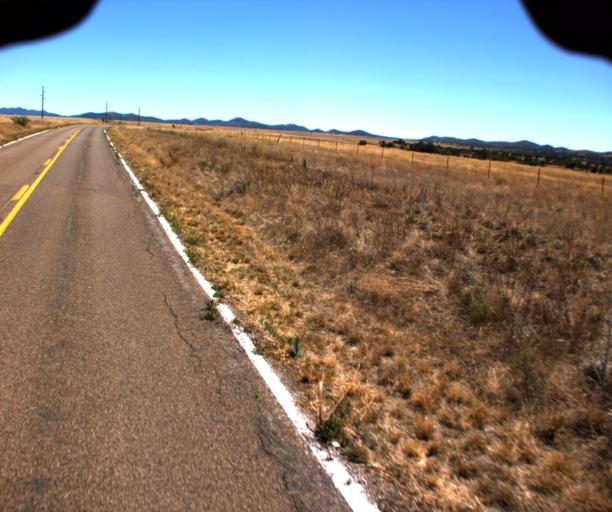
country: US
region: Arizona
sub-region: Cochise County
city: Huachuca City
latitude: 31.6477
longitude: -110.6021
